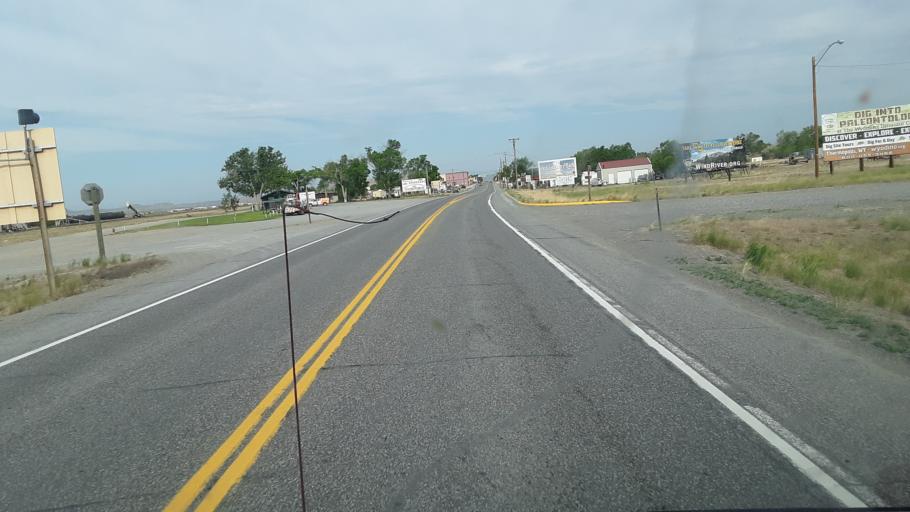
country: US
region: Wyoming
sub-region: Fremont County
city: Riverton
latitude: 43.2356
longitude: -108.1015
